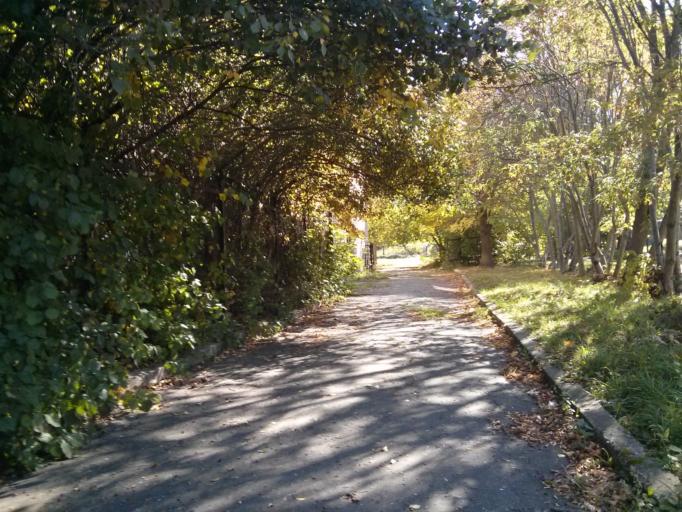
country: RU
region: Vladimir
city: Murom
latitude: 55.5519
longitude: 42.0570
